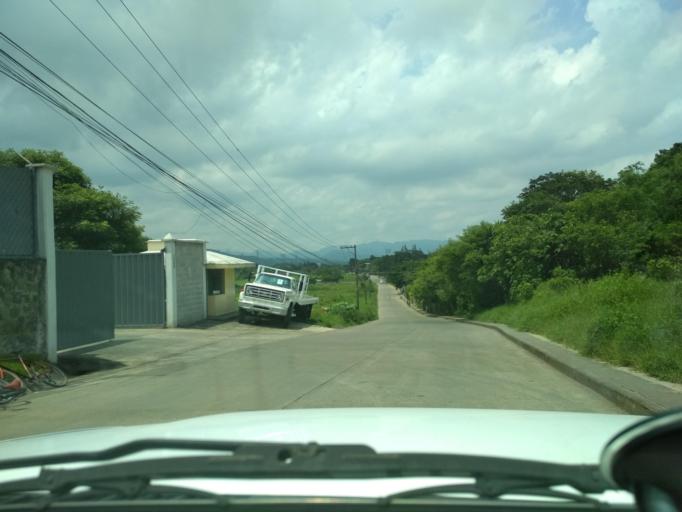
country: MX
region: Veracruz
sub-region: Ixtaczoquitlan
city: Buenavista
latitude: 18.8813
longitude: -97.0512
